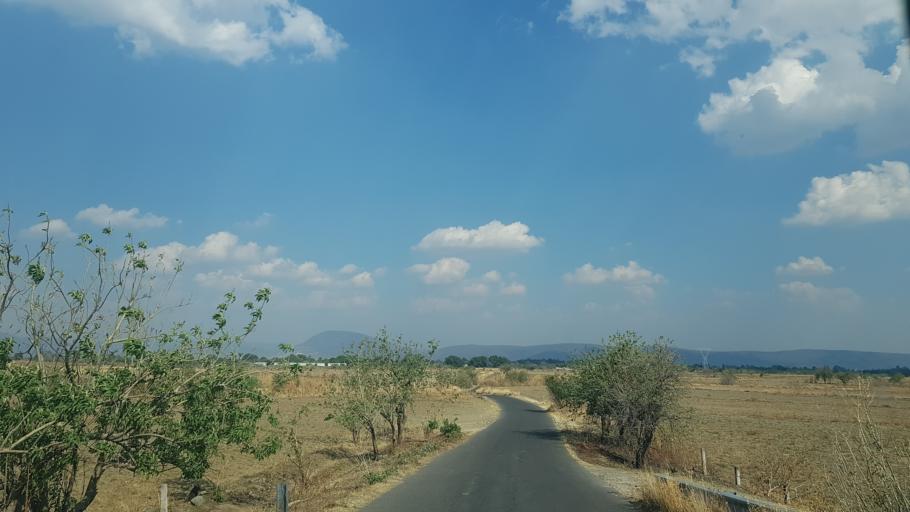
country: MX
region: Puebla
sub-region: Atlixco
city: Colonia Agricola de Ocotepec (Colonia San Jose)
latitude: 18.8866
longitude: -98.4977
